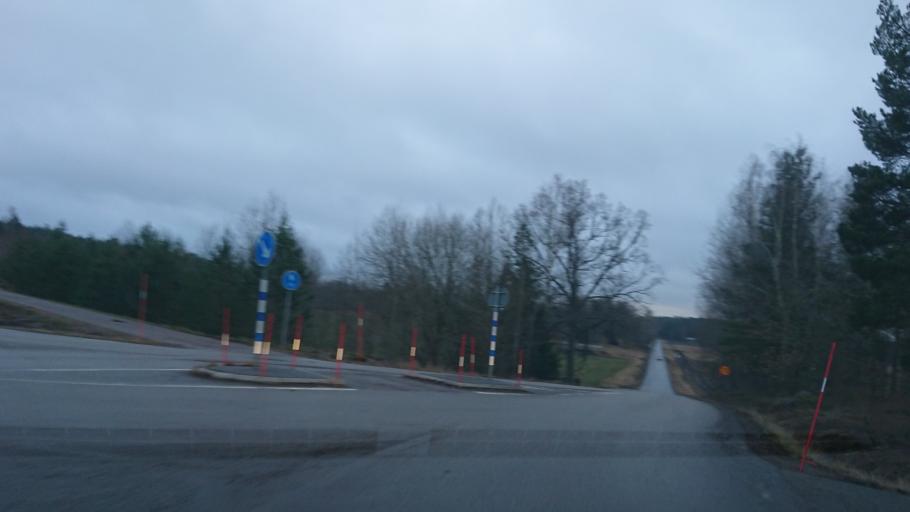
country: SE
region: Uppsala
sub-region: Osthammars Kommun
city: Bjorklinge
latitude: 60.0108
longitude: 17.5912
